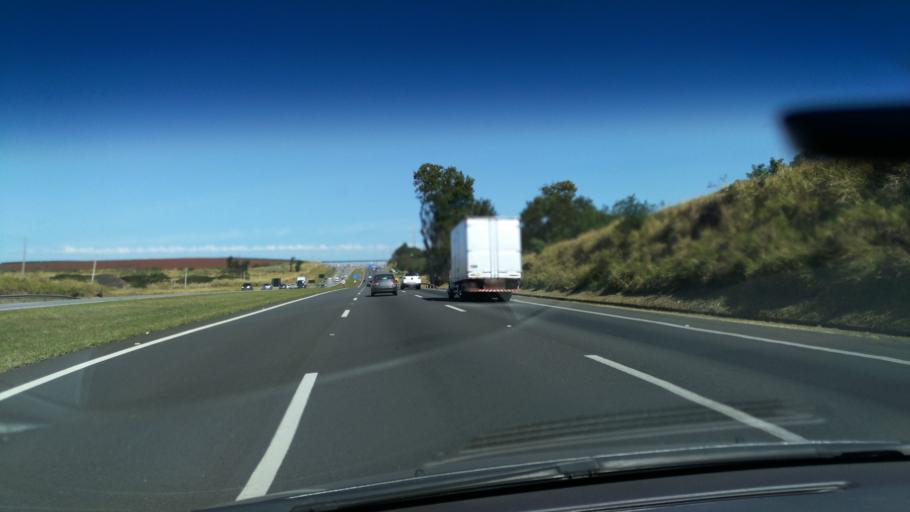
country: BR
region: Sao Paulo
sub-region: Jaguariuna
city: Jaguariuna
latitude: -22.7607
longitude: -47.0214
